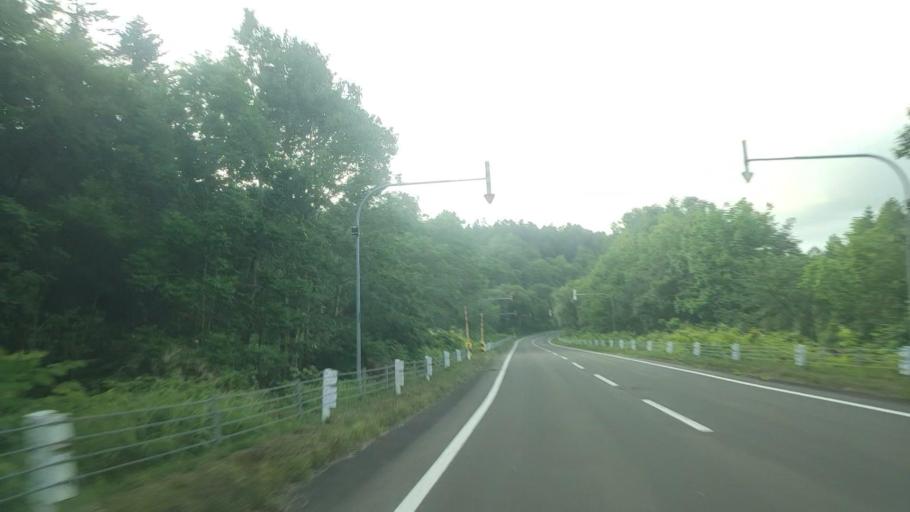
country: JP
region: Hokkaido
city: Bibai
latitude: 43.1142
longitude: 142.0995
